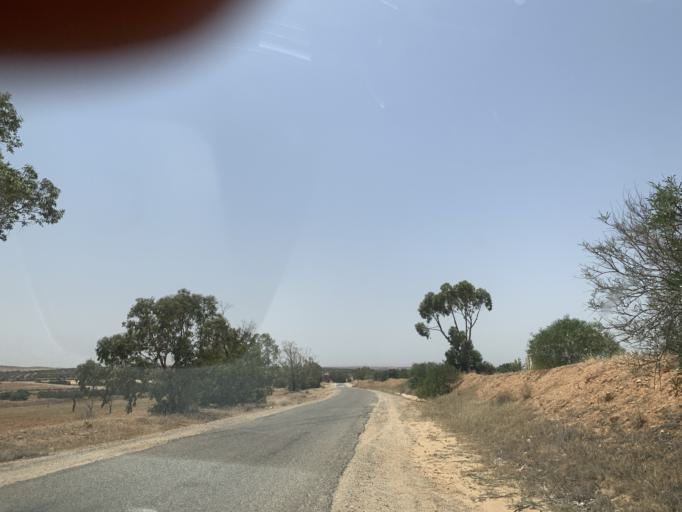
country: TN
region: Al Mahdiyah
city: Shurban
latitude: 35.1606
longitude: 10.2544
